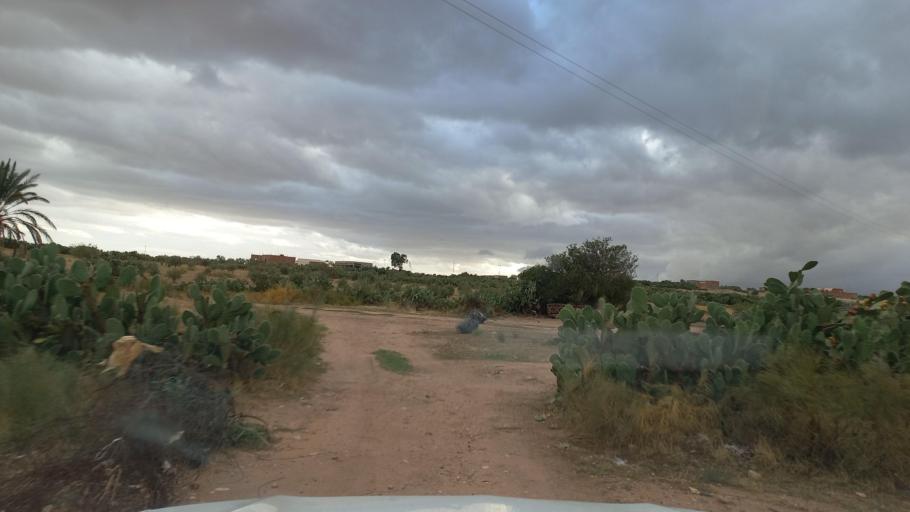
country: TN
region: Al Qasrayn
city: Kasserine
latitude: 35.2774
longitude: 8.9482
